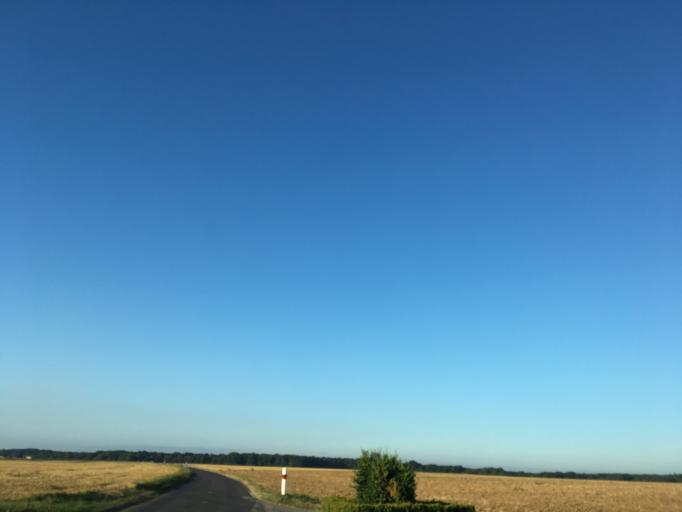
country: FR
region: Haute-Normandie
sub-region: Departement de l'Eure
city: Heudreville-sur-Eure
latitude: 49.1572
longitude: 1.2410
